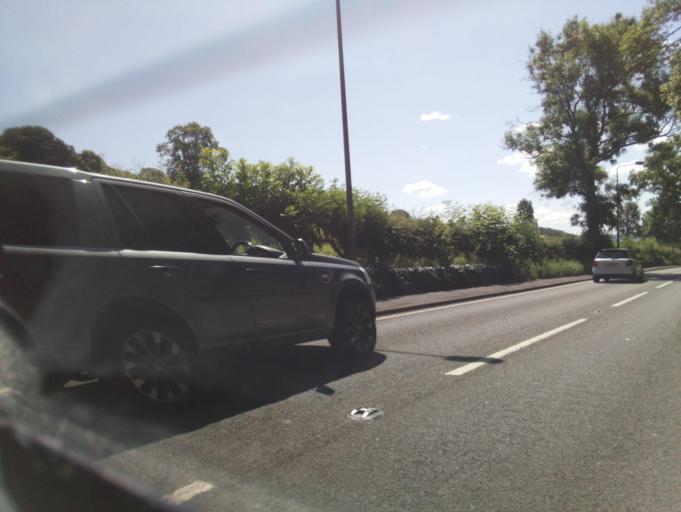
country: GB
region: England
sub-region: Derbyshire
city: Bakewell
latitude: 53.1838
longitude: -1.6110
